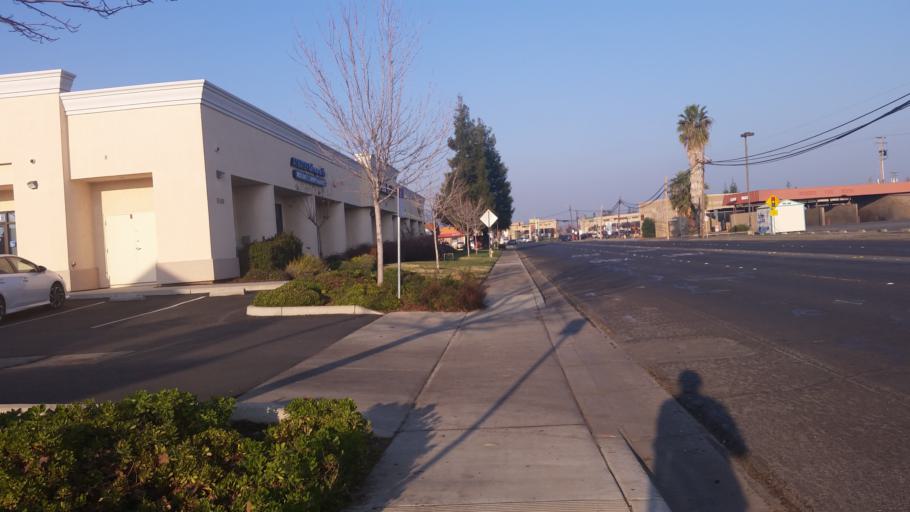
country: US
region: California
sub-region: Merced County
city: Atwater
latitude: 37.3589
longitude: -120.5973
